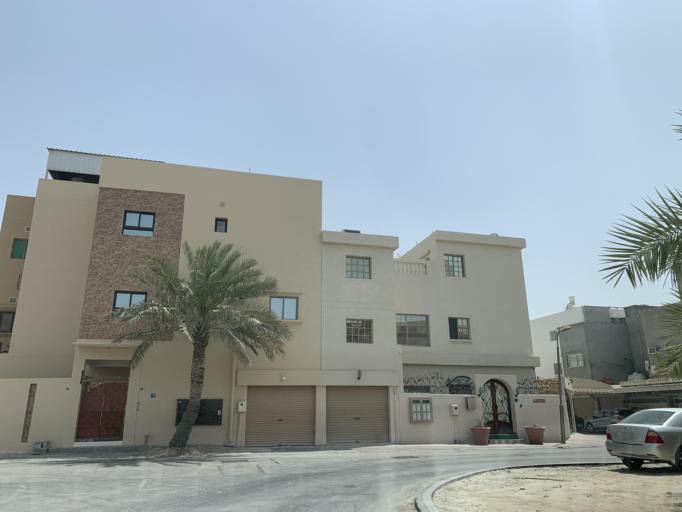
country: BH
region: Northern
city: Madinat `Isa
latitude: 26.1625
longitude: 50.5260
